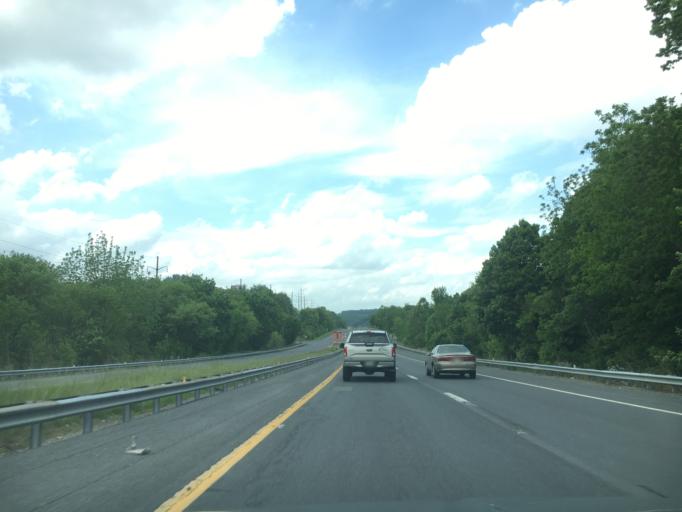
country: US
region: Pennsylvania
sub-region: Lehigh County
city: Cementon
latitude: 40.6952
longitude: -75.5230
